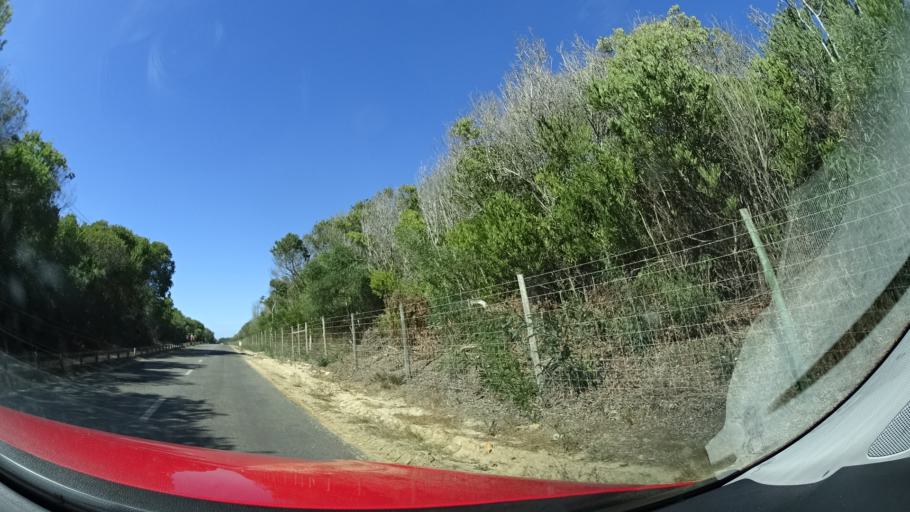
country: PT
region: Beja
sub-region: Odemira
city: Sao Teotonio
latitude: 37.5403
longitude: -8.7866
